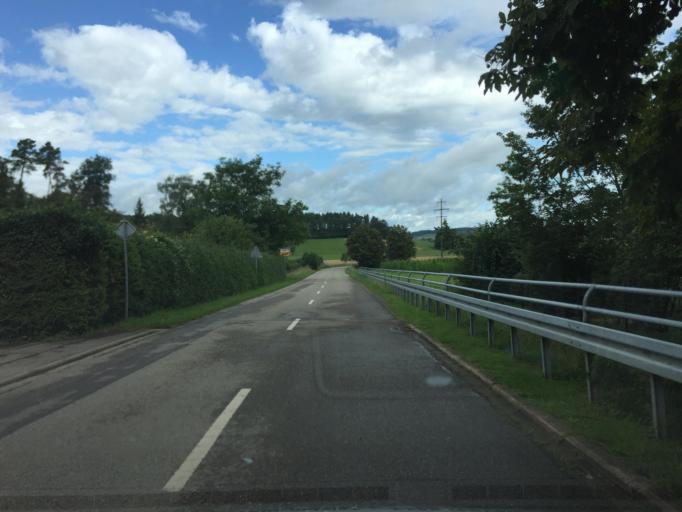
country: CH
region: Schaffhausen
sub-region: Bezirk Unterklettgau
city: Wilchingen
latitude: 47.6455
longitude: 8.4572
